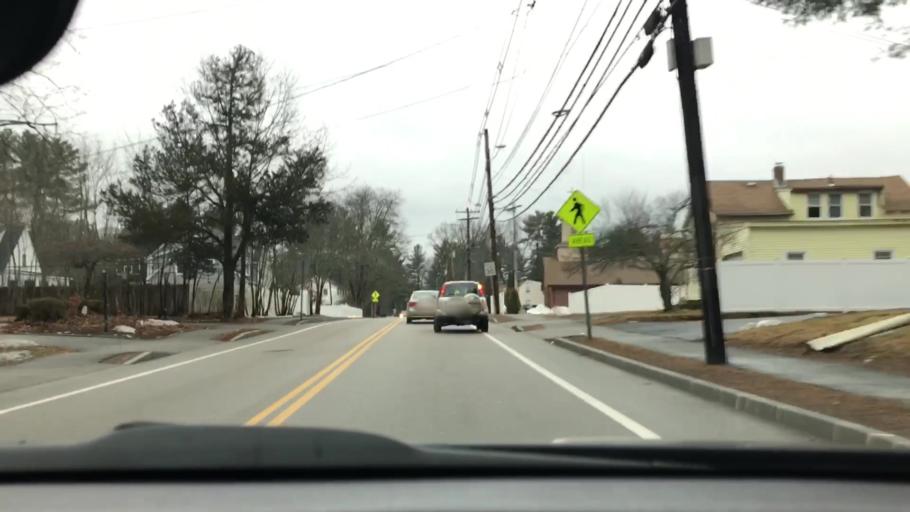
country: US
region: Massachusetts
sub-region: Middlesex County
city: Natick
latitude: 42.3089
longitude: -71.3334
